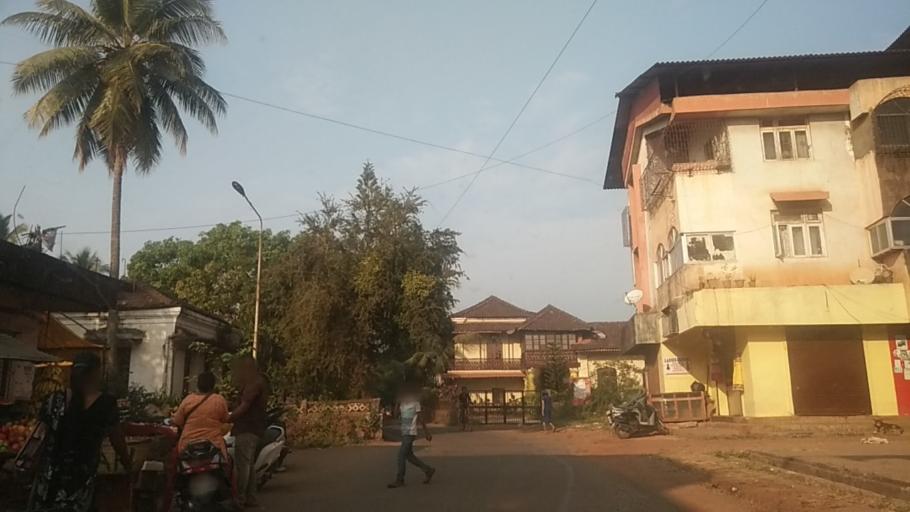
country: IN
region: Goa
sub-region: South Goa
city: Madgaon
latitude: 15.2649
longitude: 73.9597
